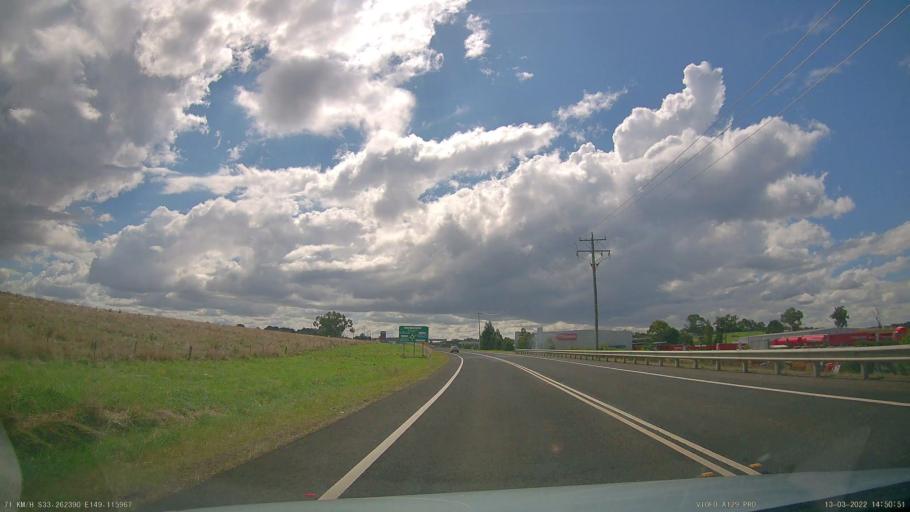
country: AU
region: New South Wales
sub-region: Orange Municipality
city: Orange
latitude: -33.2625
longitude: 149.1161
